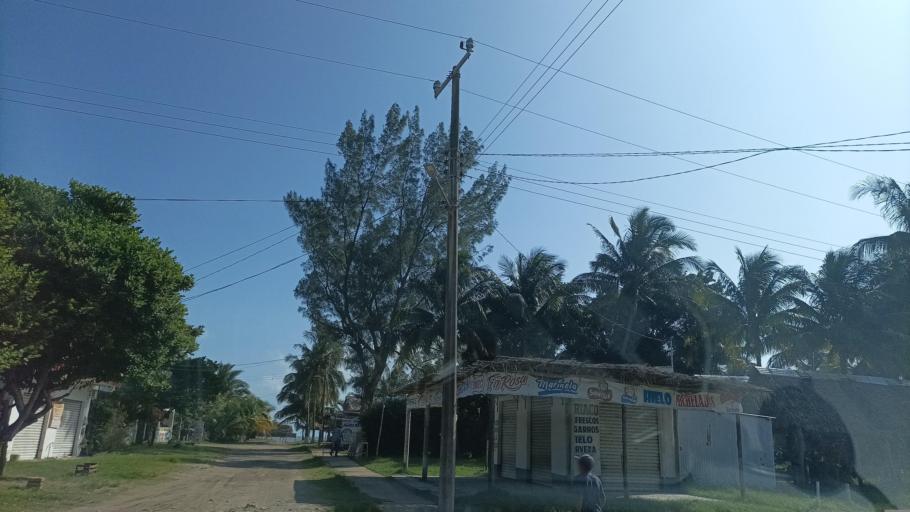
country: MX
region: Veracruz
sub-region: Coatzacoalcos
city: Fraccionamiento Ciudad Olmeca
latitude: 18.2117
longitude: -94.6114
